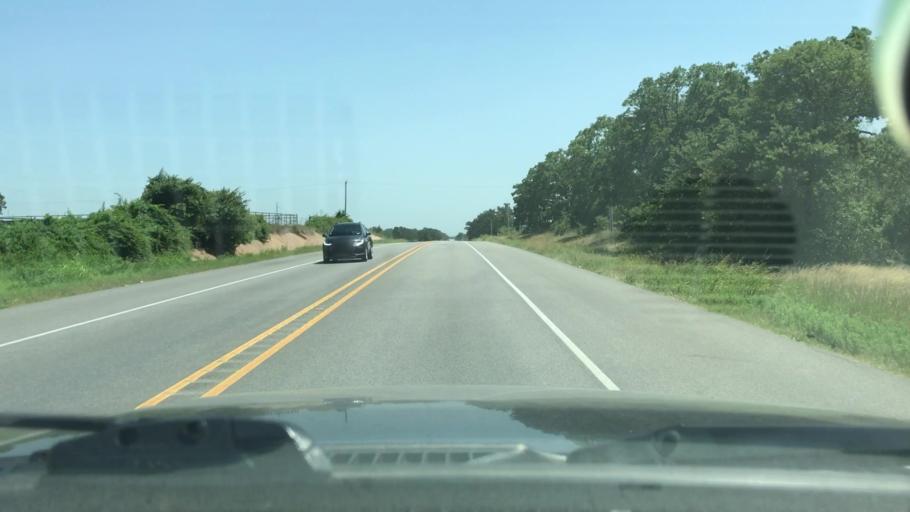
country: US
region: Texas
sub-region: Bastrop County
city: Camp Swift
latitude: 30.1843
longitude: -97.3154
